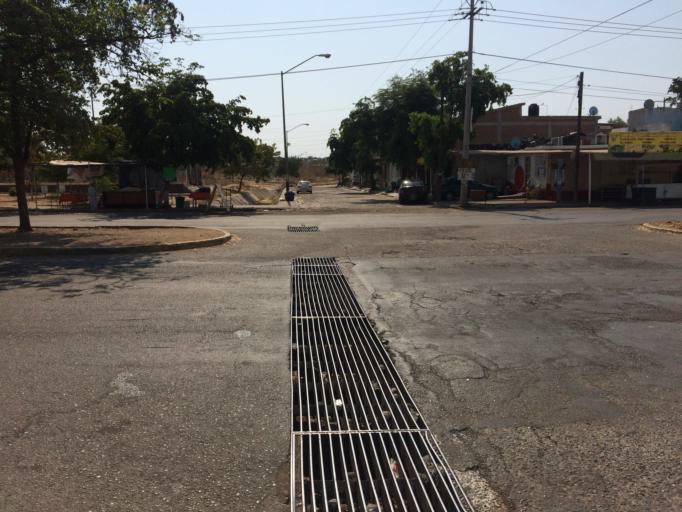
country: MX
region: Sinaloa
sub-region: Culiacan
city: El Diez
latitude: 24.7559
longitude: -107.4292
